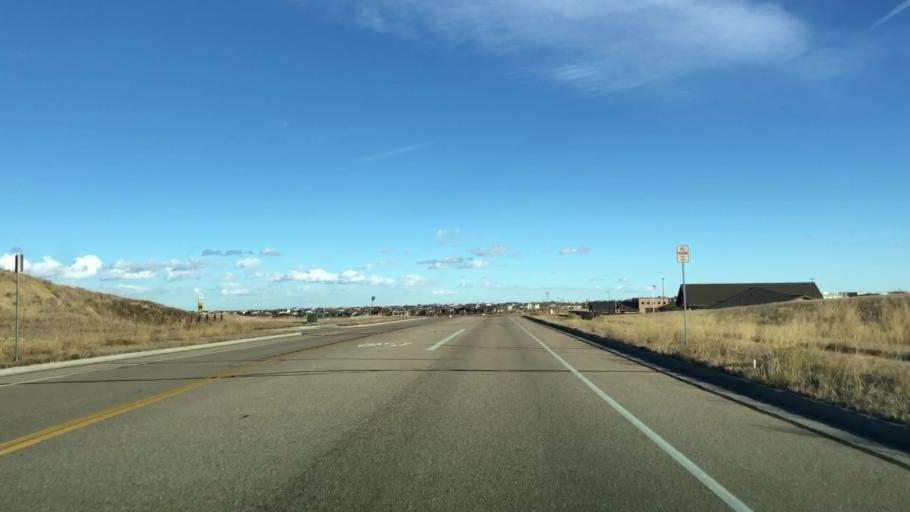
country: US
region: Colorado
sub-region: Weld County
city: Windsor
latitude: 40.4431
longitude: -104.9810
